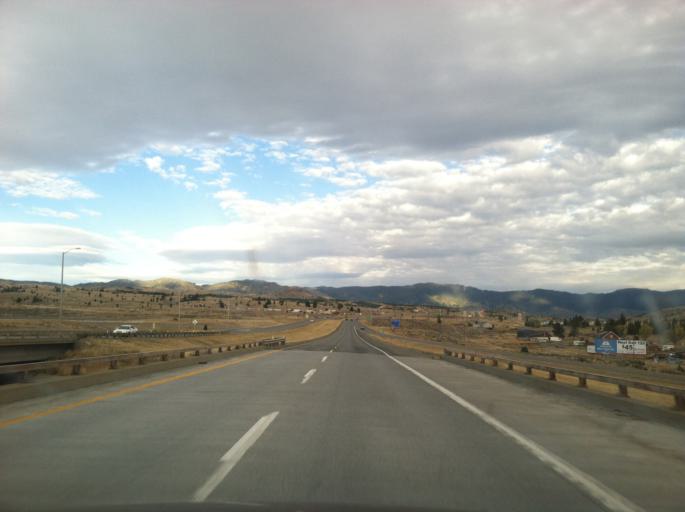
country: US
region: Montana
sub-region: Silver Bow County
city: Butte
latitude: 46.0080
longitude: -112.6387
